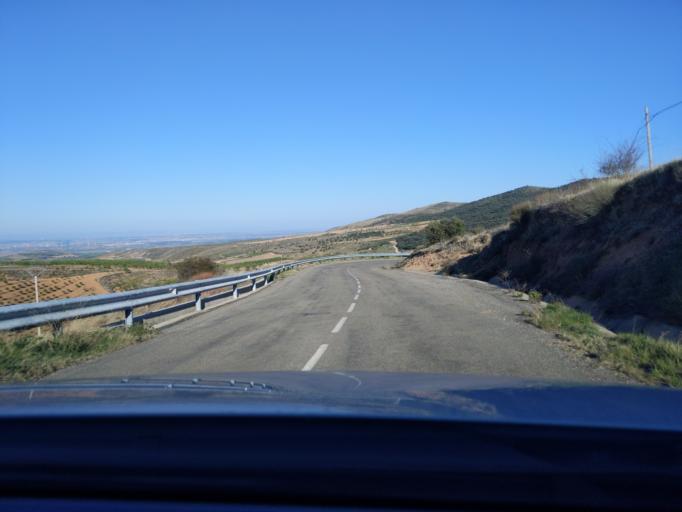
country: ES
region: La Rioja
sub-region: Provincia de La Rioja
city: Bergasillas Bajera
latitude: 42.2462
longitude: -2.1470
